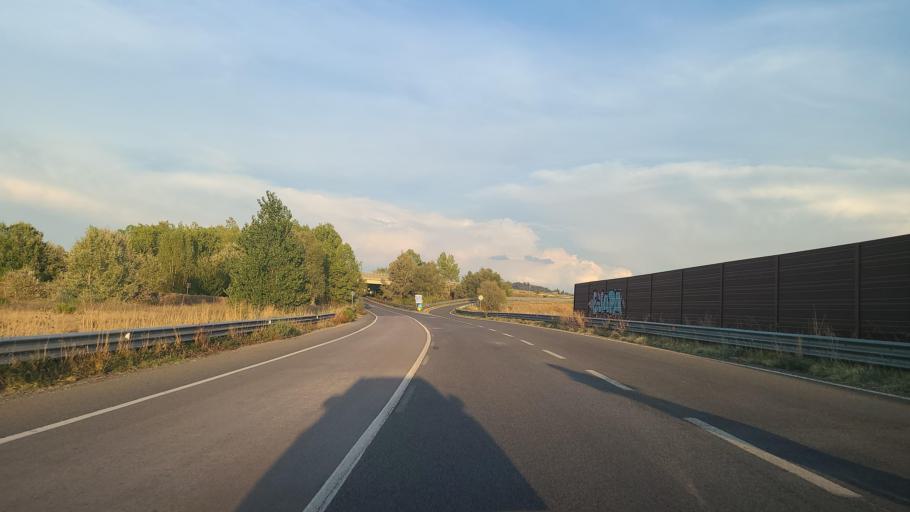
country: IT
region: Tuscany
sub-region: Provincia di Siena
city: Poggibonsi
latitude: 43.4825
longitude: 11.1237
